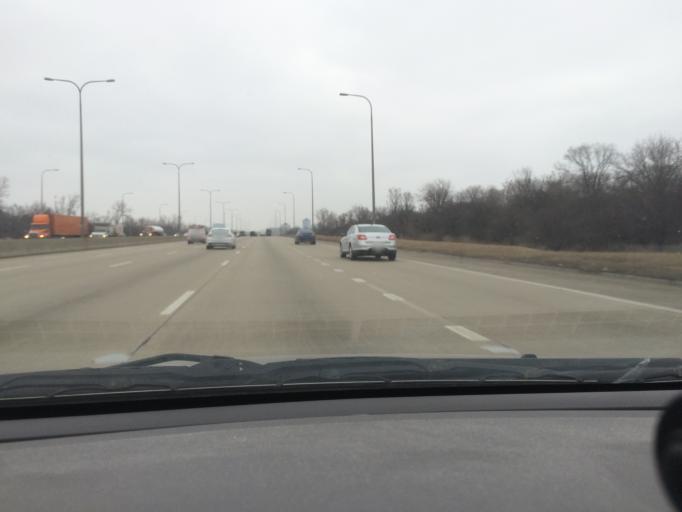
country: US
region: Illinois
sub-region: DuPage County
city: Itasca
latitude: 42.0064
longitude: -88.0275
